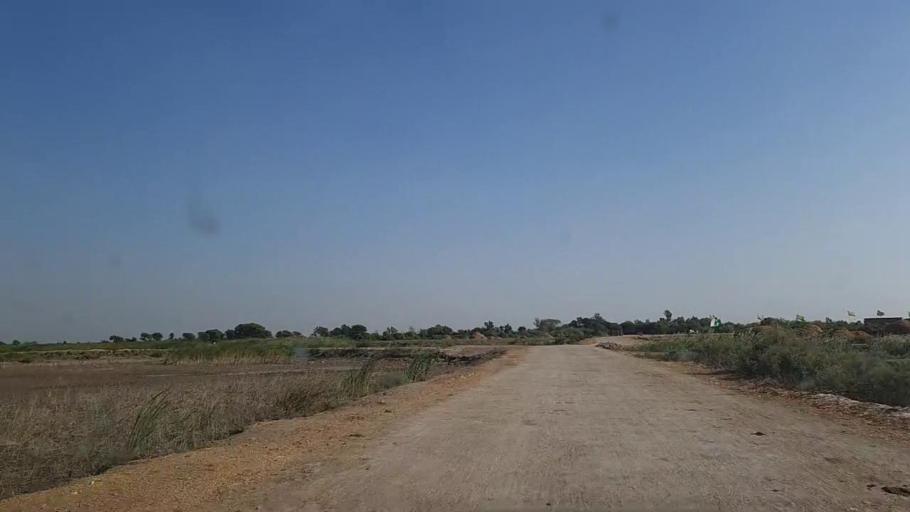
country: PK
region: Sindh
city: Daro Mehar
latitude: 24.6272
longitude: 68.0792
